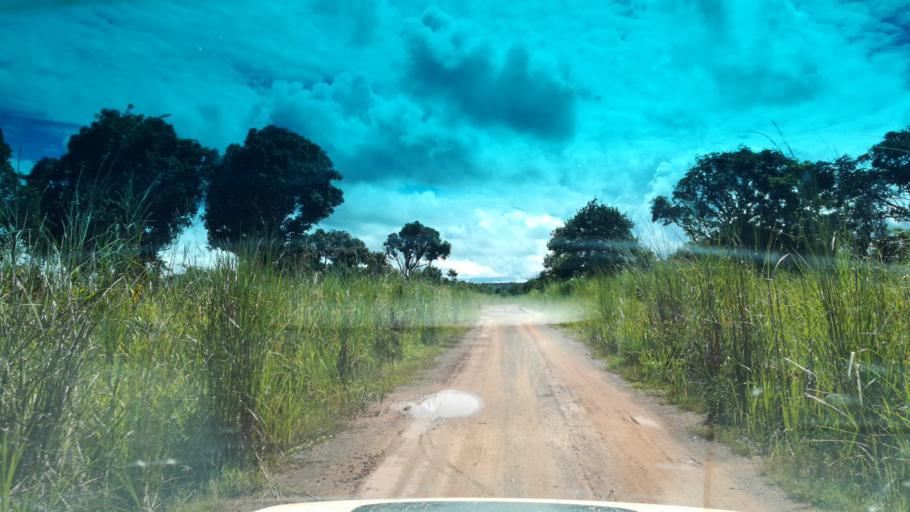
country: ZM
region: Northern
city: Kaputa
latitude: -7.7814
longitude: 29.2197
